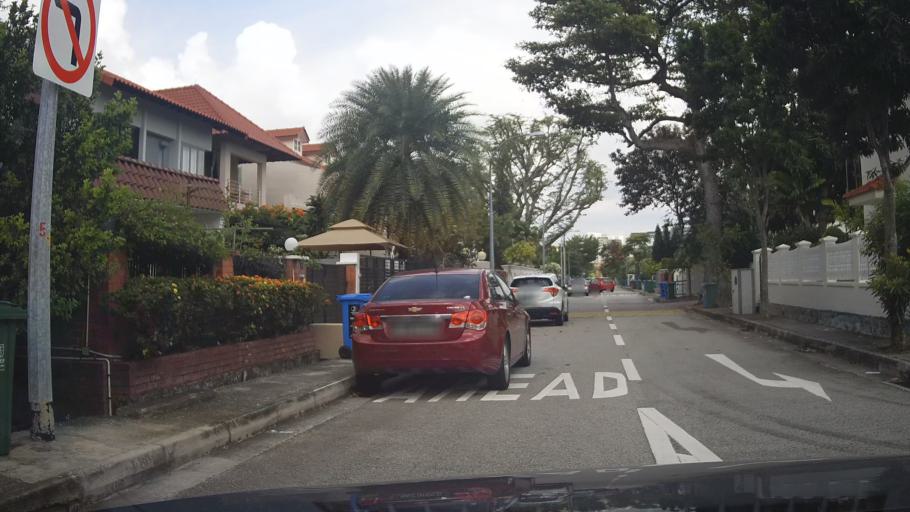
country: SG
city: Singapore
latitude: 1.3111
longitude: 103.9173
